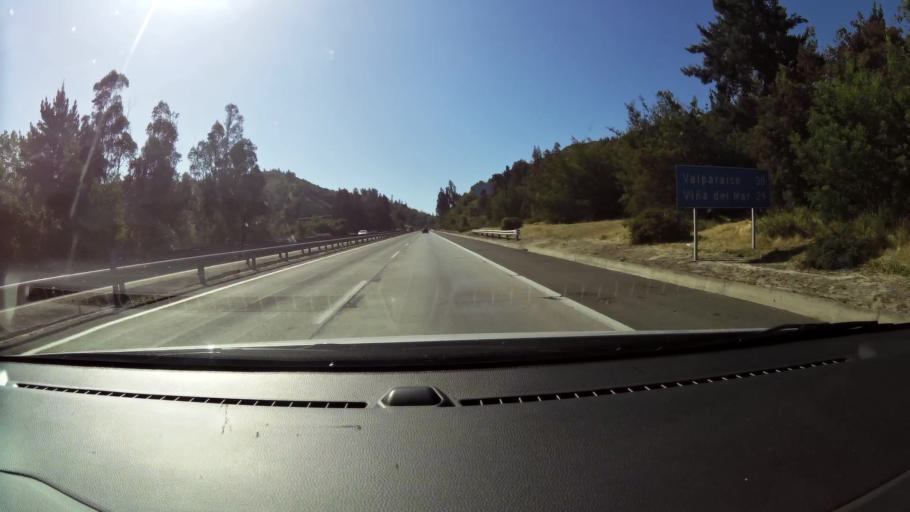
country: CL
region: Valparaiso
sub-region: Provincia de Marga Marga
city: Quilpue
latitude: -33.2396
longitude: -71.4552
